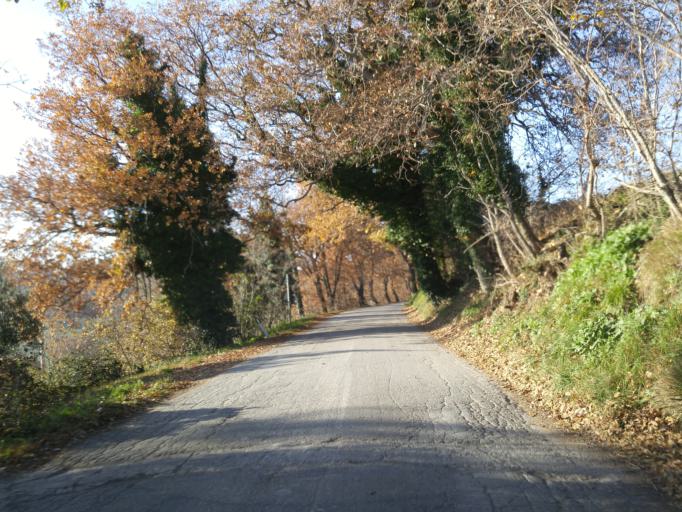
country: IT
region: The Marches
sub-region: Provincia di Pesaro e Urbino
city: Montefelcino
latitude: 43.7434
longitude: 12.8319
